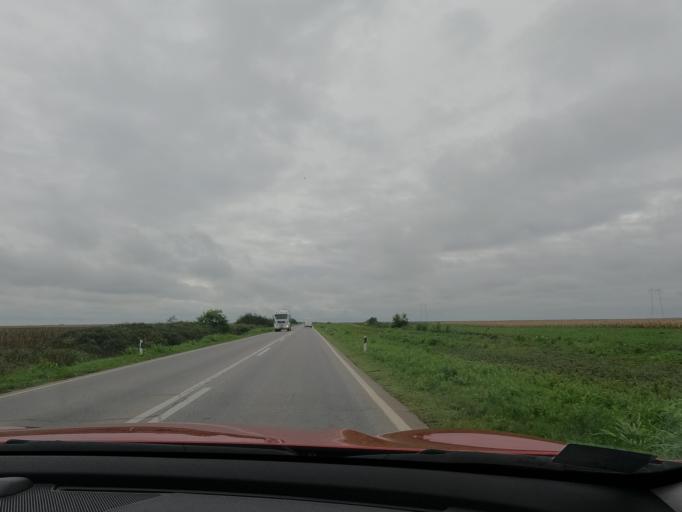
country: RS
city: Elemir
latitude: 45.4697
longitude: 20.3406
